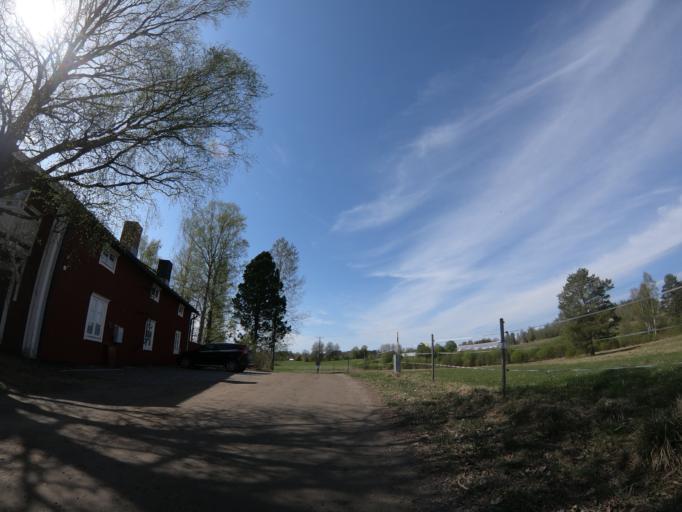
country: SE
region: Vaesterbotten
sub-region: Umea Kommun
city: Roback
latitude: 63.8292
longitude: 20.1922
